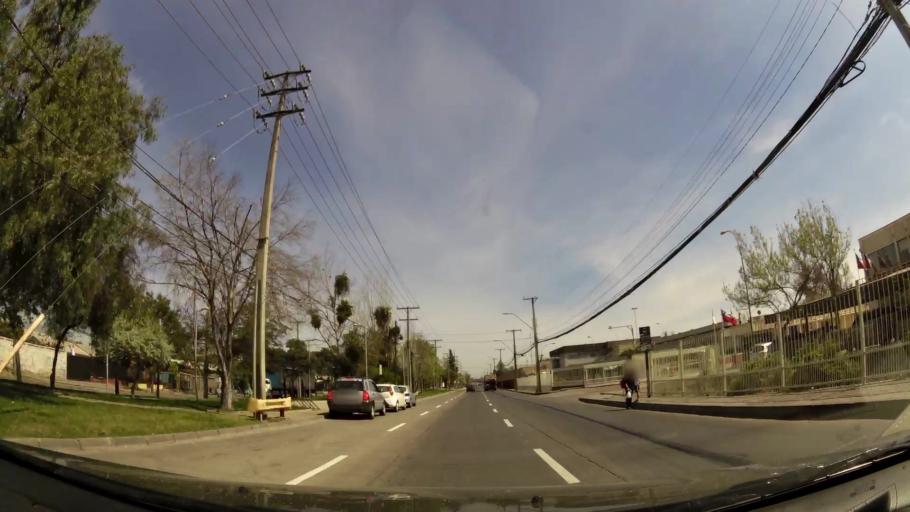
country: CL
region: Santiago Metropolitan
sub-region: Provincia de Cordillera
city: Puente Alto
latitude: -33.6113
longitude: -70.5648
